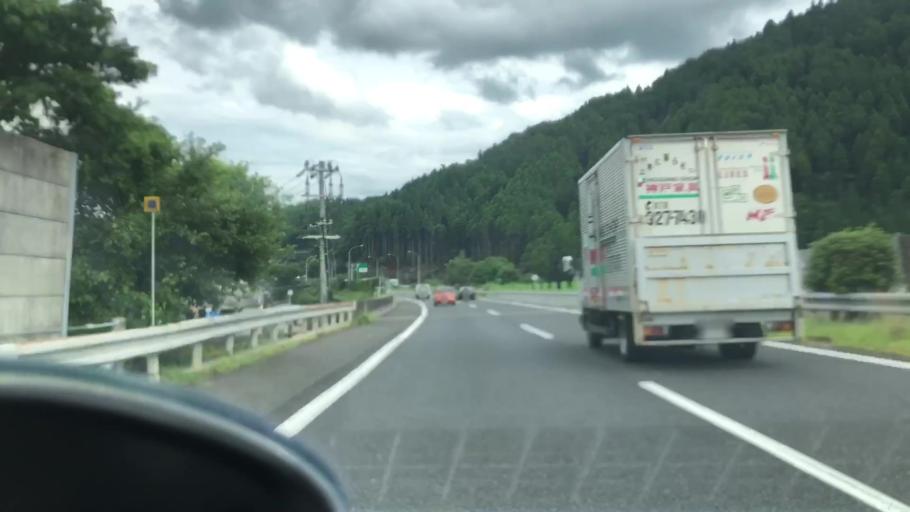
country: JP
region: Hyogo
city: Yamazakicho-nakabirose
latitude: 34.9866
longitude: 134.5985
